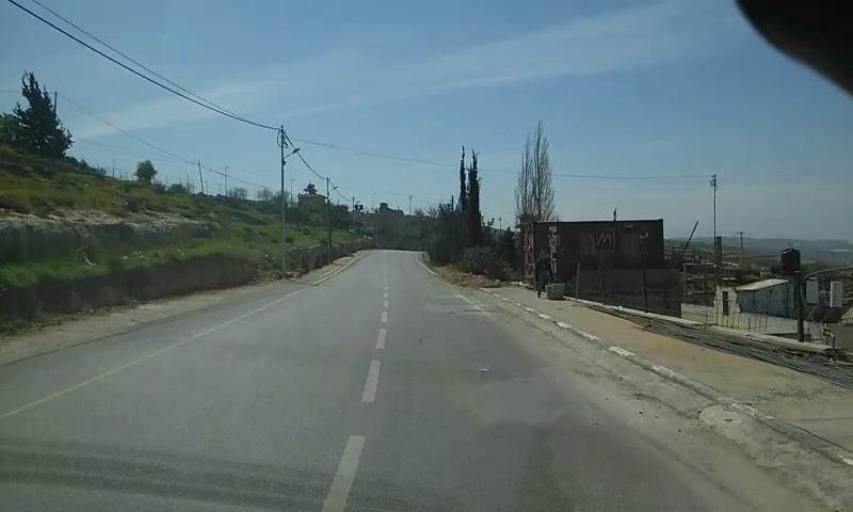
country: PS
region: West Bank
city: Husan
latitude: 31.7064
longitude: 35.1458
